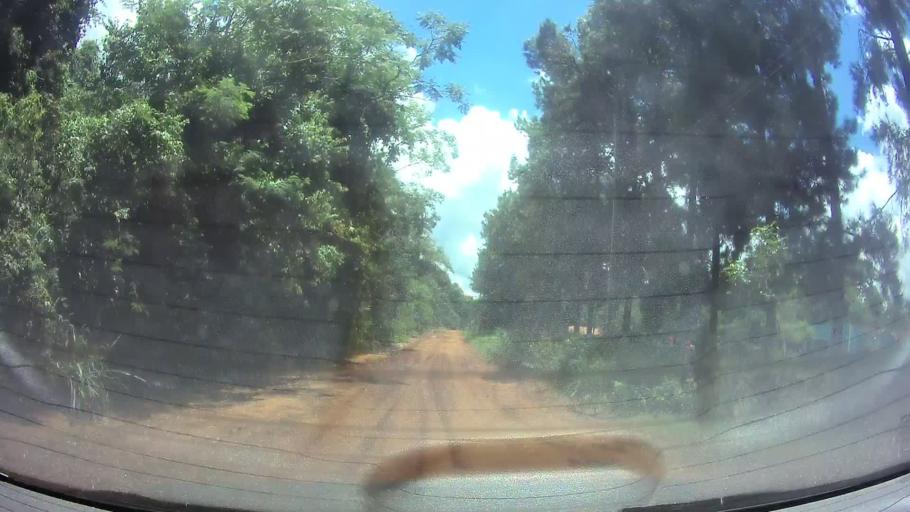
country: PY
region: Paraguari
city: La Colmena
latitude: -25.9168
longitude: -56.7949
